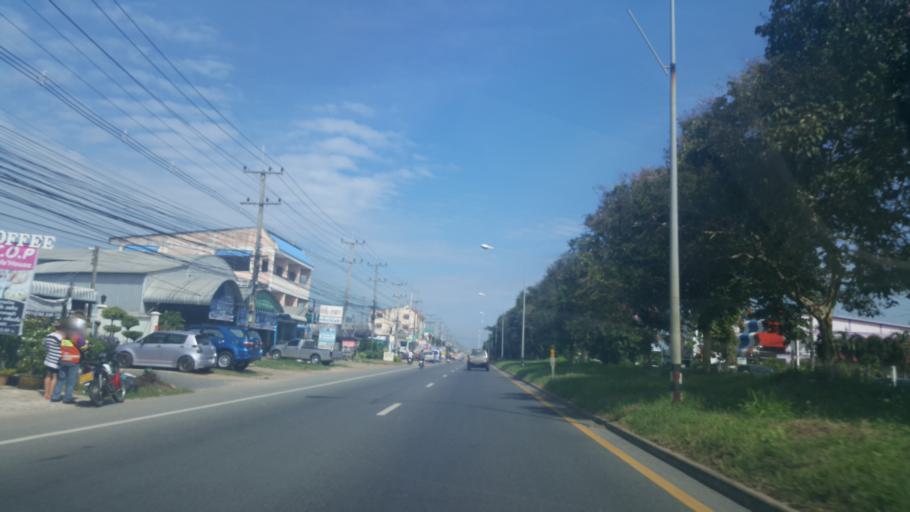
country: TH
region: Chon Buri
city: Sattahip
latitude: 12.6927
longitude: 100.8919
